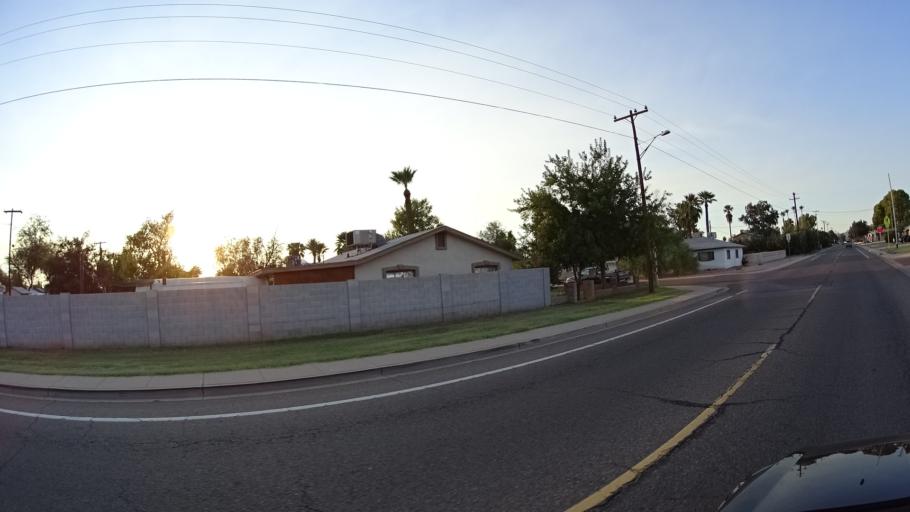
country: US
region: Arizona
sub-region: Maricopa County
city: Phoenix
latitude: 33.4898
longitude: -112.0389
